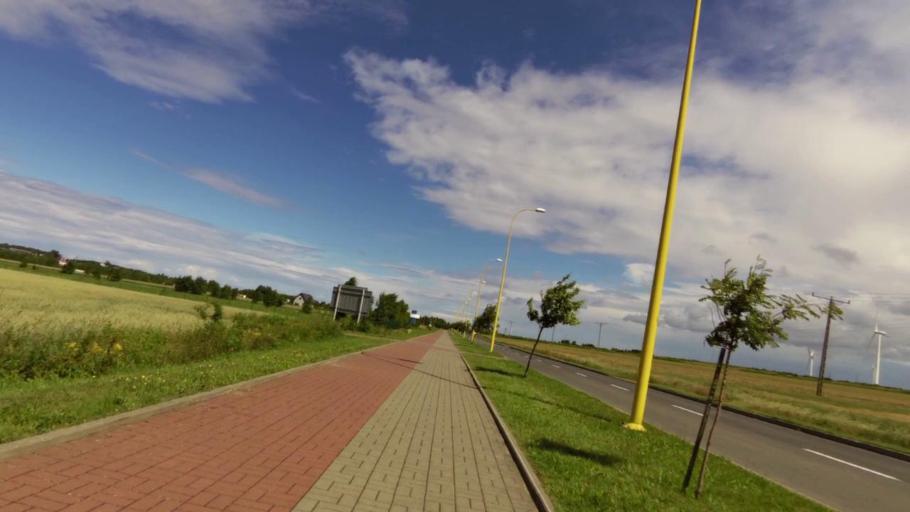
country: PL
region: West Pomeranian Voivodeship
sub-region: Powiat slawienski
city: Darlowo
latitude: 54.4385
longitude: 16.4084
